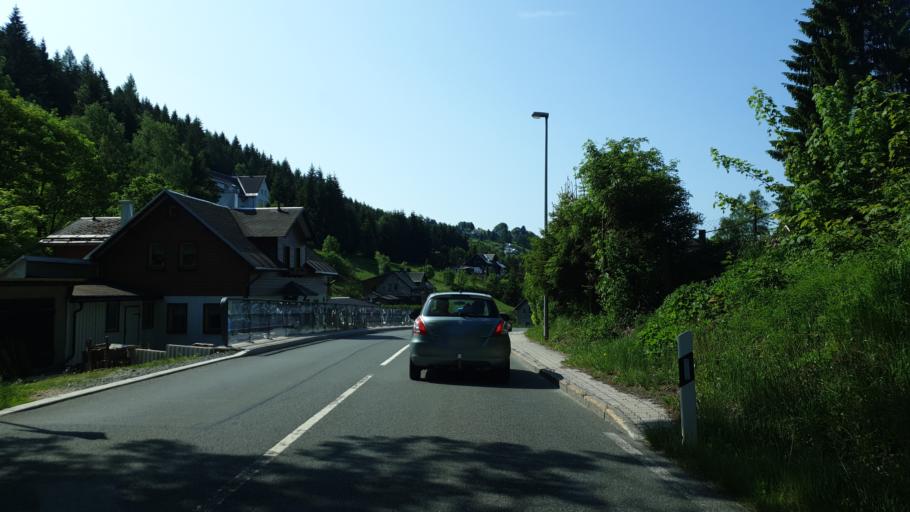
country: DE
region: Saxony
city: Klingenthal
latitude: 50.3968
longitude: 12.4957
